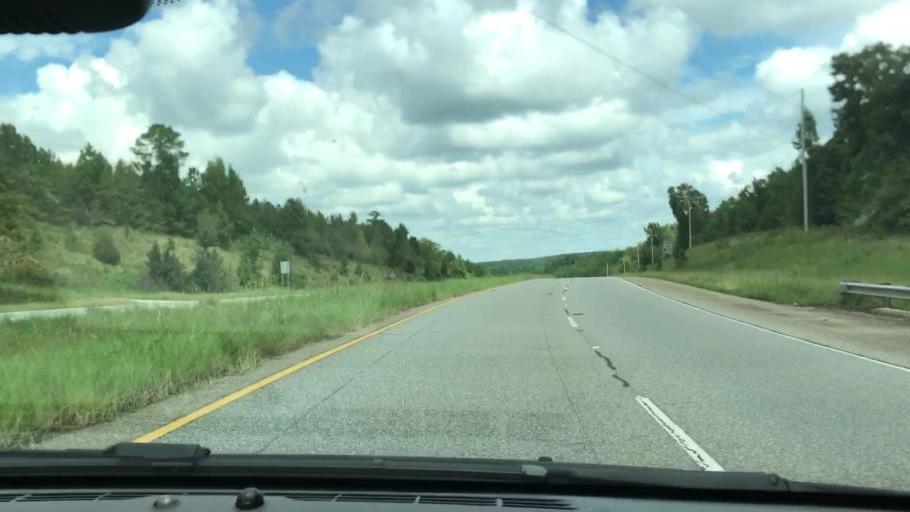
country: US
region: Georgia
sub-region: Stewart County
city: Lumpkin
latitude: 32.0906
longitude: -84.8098
